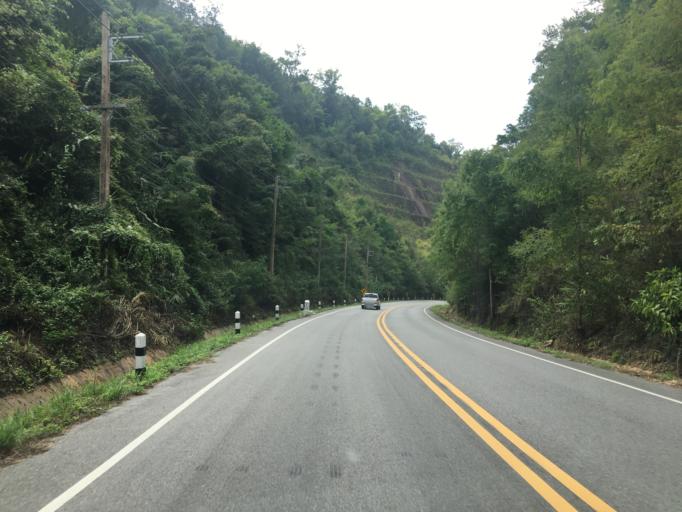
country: TH
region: Nan
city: Ban Luang
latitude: 18.8721
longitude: 100.4834
